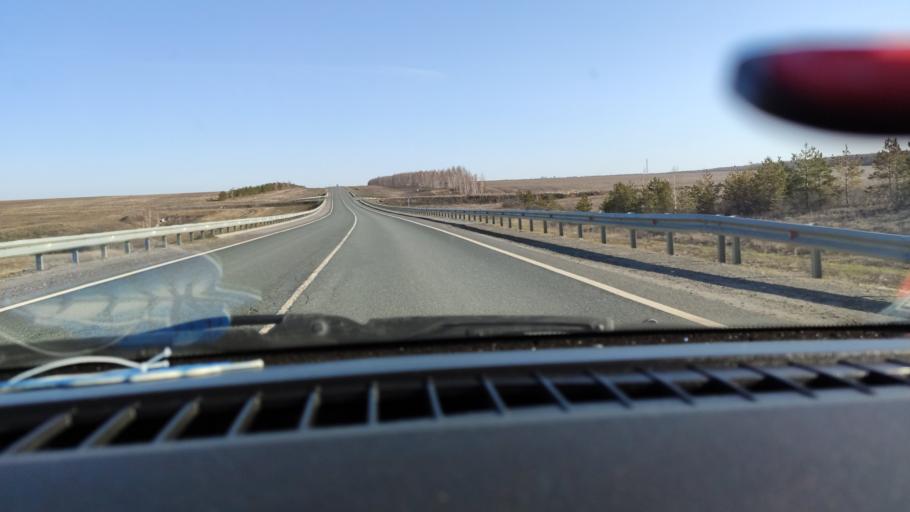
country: RU
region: Samara
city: Syzran'
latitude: 52.8859
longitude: 48.2938
